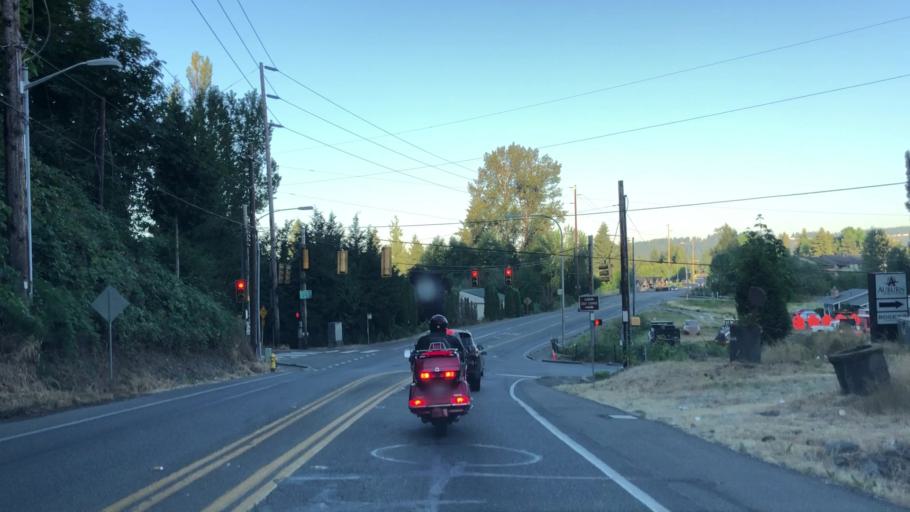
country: US
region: Washington
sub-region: King County
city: Lea Hill
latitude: 47.3157
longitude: -122.2031
